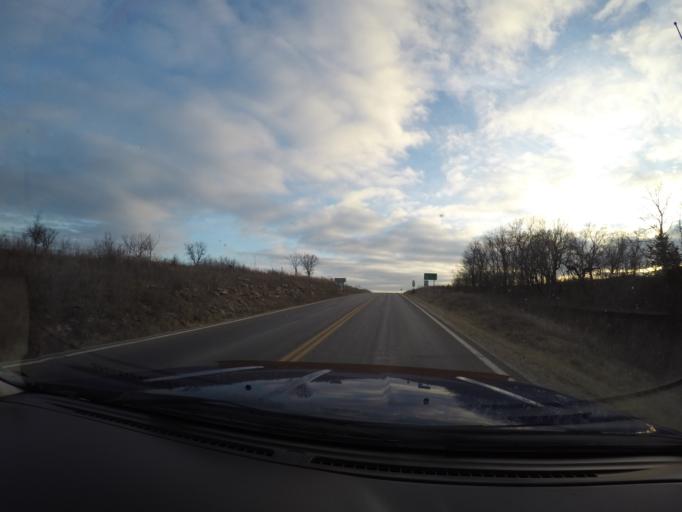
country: US
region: Kansas
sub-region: Morris County
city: Council Grove
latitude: 38.6485
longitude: -96.4892
